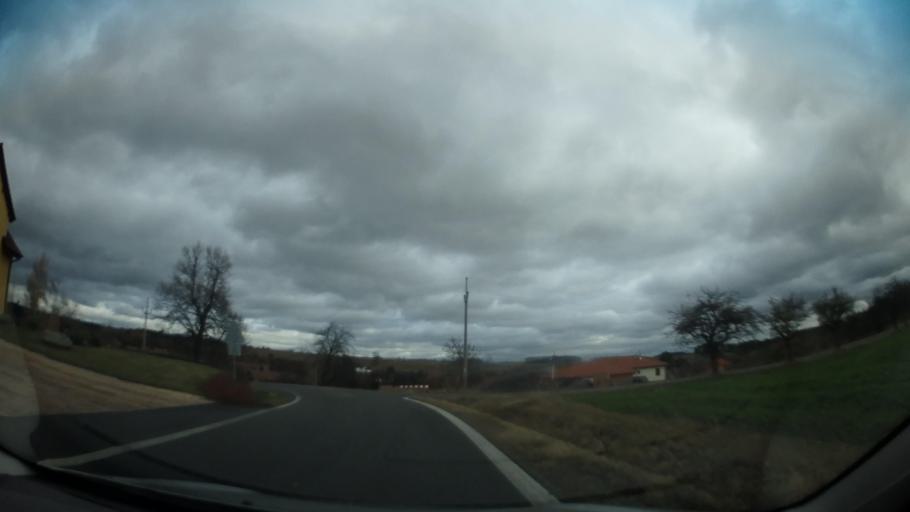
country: CZ
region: Vysocina
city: Namest' nad Oslavou
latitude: 49.2904
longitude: 16.1363
